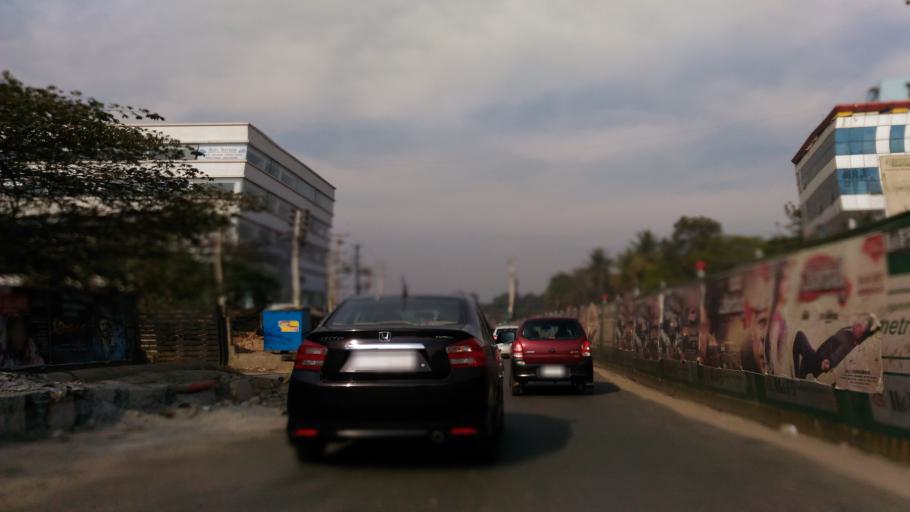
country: IN
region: Karnataka
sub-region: Bangalore Urban
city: Bangalore
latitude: 12.9363
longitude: 77.5170
